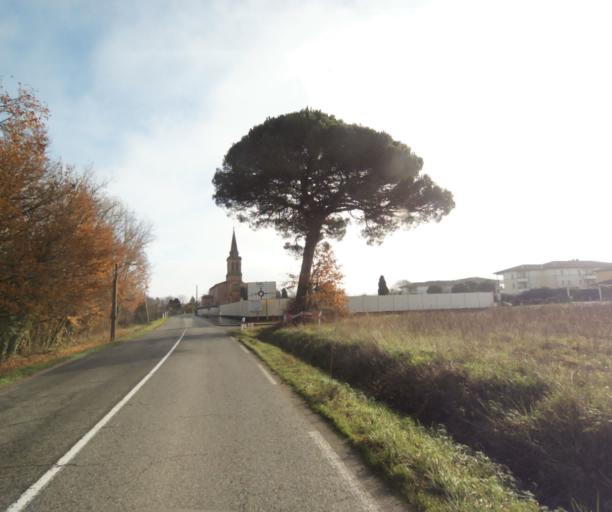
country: FR
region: Midi-Pyrenees
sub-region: Departement de la Haute-Garonne
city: Villemur-sur-Tarn
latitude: 43.8624
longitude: 1.4793
